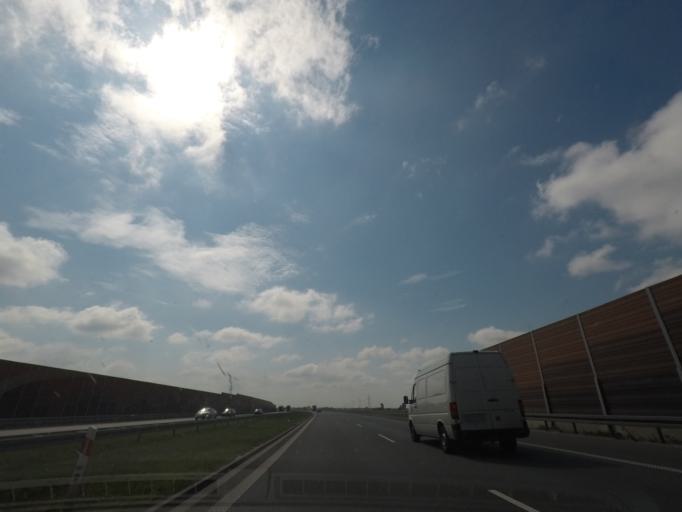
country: PL
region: Kujawsko-Pomorskie
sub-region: Powiat wloclawski
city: Lubanie
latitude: 52.7317
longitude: 18.8602
